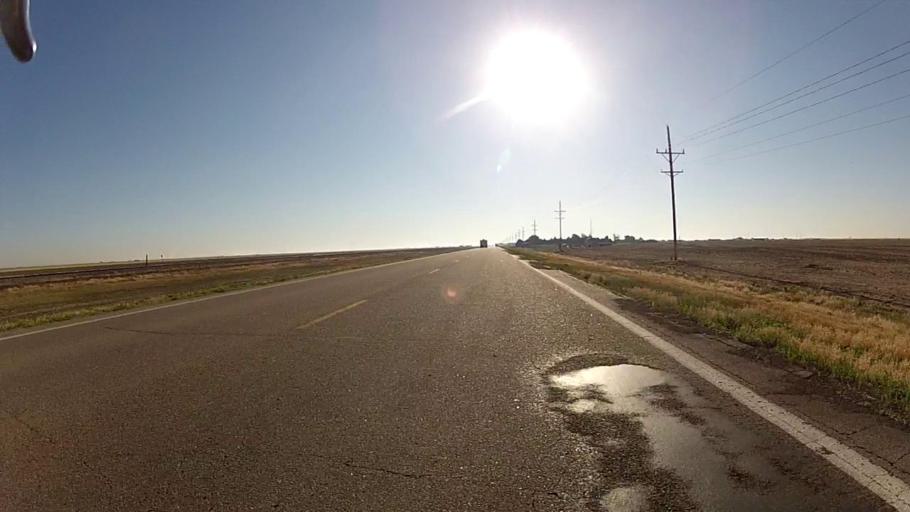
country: US
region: Kansas
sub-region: Haskell County
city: Sublette
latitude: 37.4921
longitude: -100.8127
